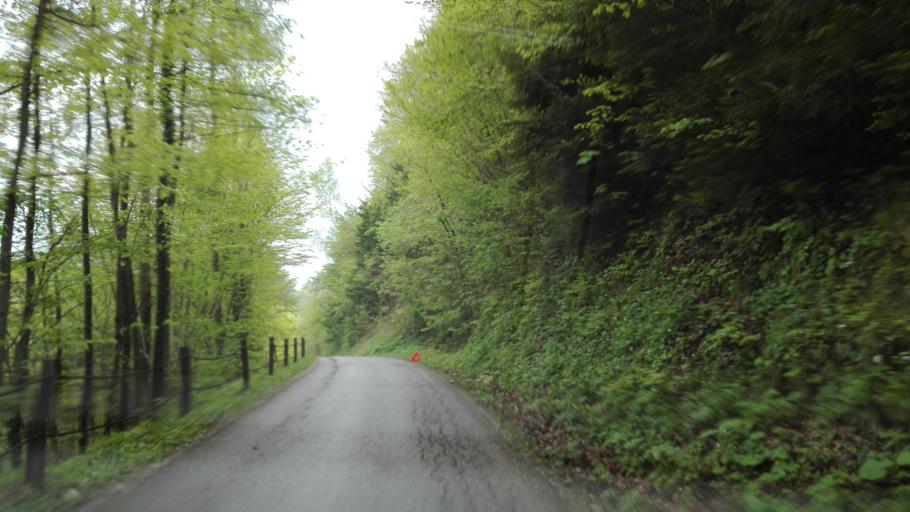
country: AT
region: Upper Austria
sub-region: Politischer Bezirk Steyr-Land
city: Ternberg
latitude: 47.9267
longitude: 14.3788
